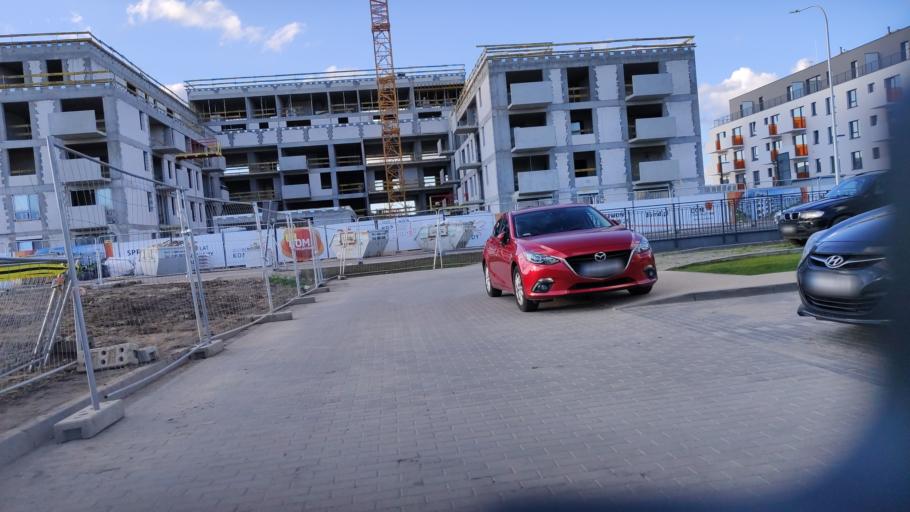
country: PL
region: Lower Silesian Voivodeship
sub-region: Powiat wroclawski
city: Zerniki Wroclawskie
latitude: 51.0555
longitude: 17.0524
